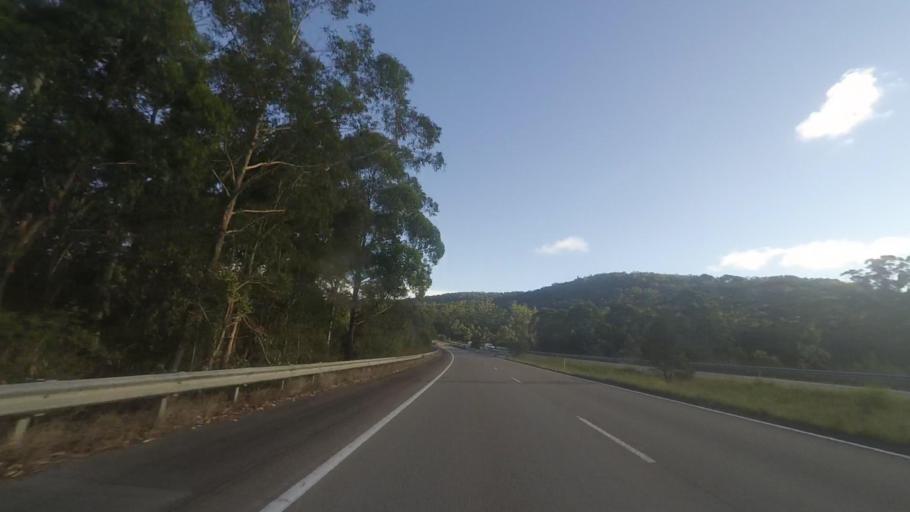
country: AU
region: New South Wales
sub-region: Great Lakes
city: Bulahdelah
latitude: -32.2718
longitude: 152.3285
